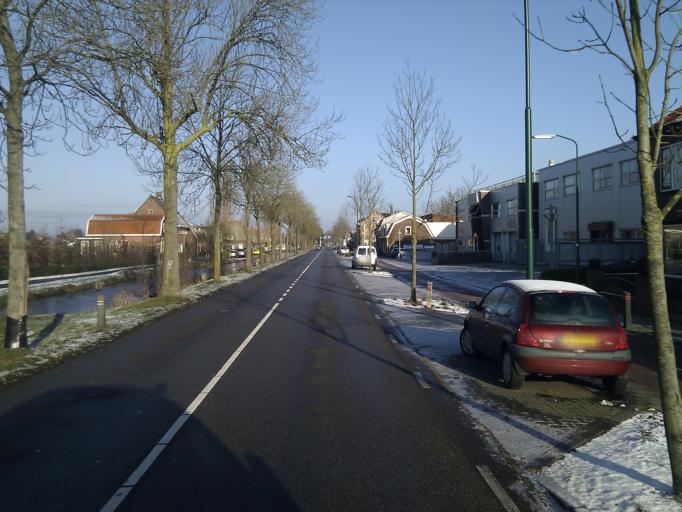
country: NL
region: Utrecht
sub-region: Gemeente Utrecht
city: Utrecht
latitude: 52.1217
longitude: 5.1422
